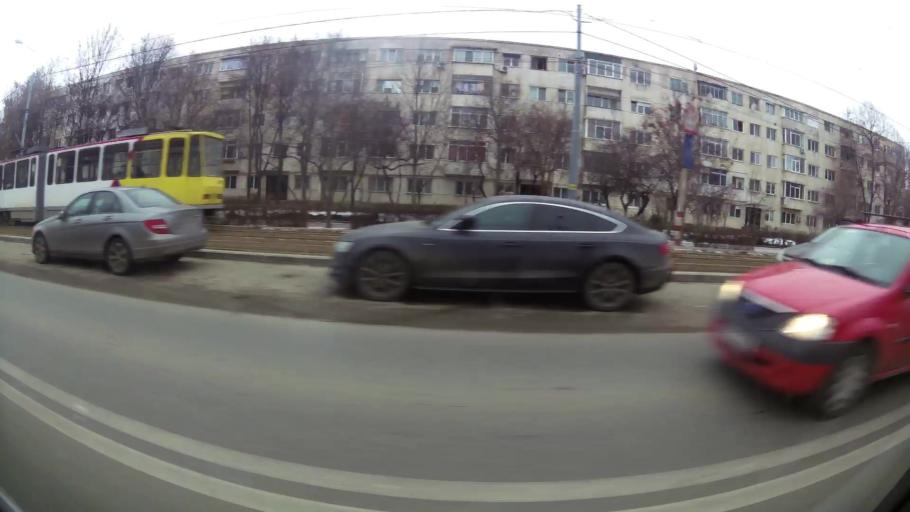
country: RO
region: Prahova
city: Ploiesti
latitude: 44.9299
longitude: 26.0322
